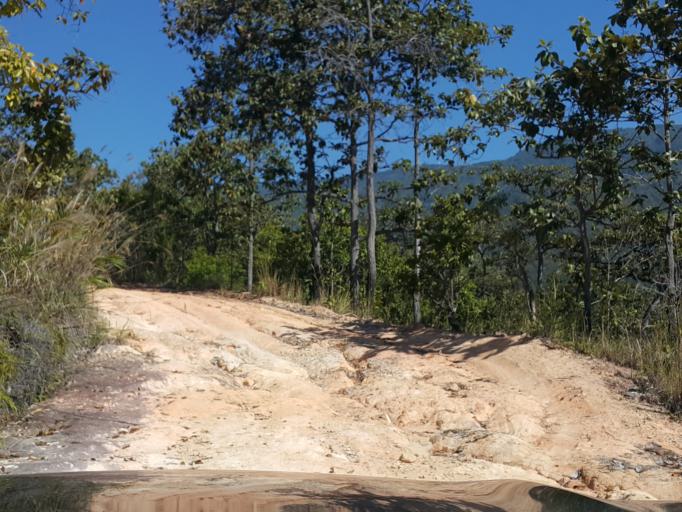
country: TH
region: Chiang Mai
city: Hang Dong
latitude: 18.7881
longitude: 98.8665
